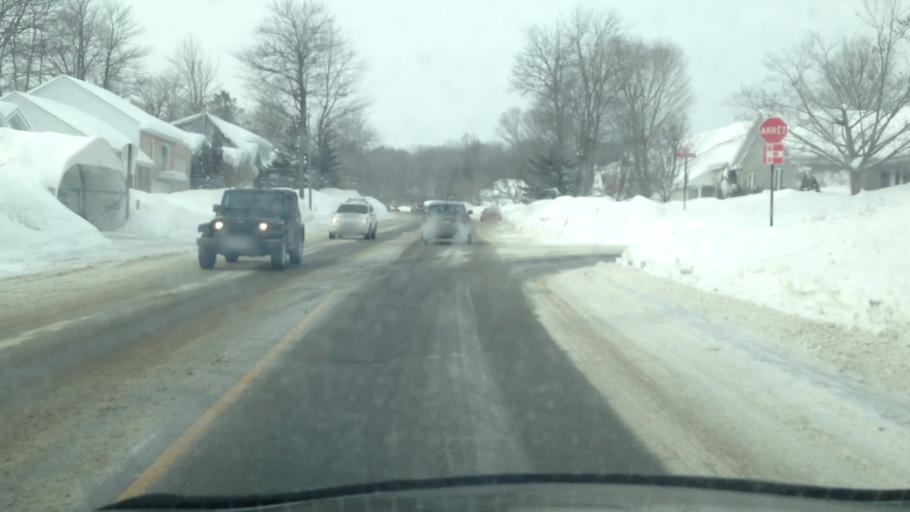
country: CA
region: Quebec
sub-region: Laurentides
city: Saint-Jerome
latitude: 45.7945
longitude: -74.0384
